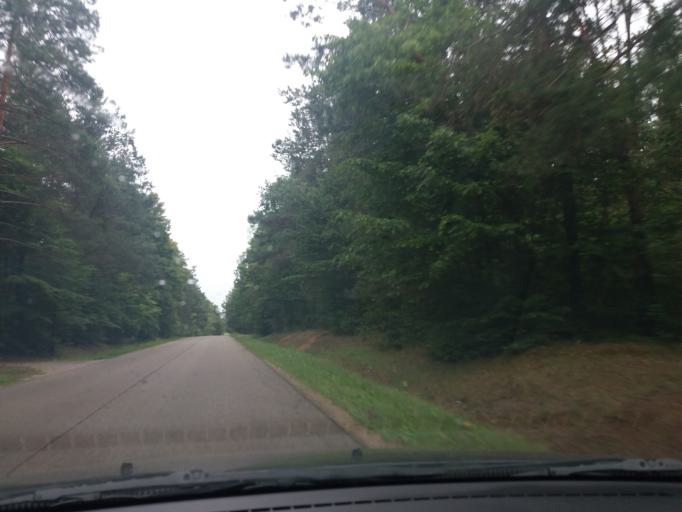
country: PL
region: Masovian Voivodeship
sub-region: Powiat mlawski
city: Wieczfnia Koscielna
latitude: 53.2053
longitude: 20.4963
